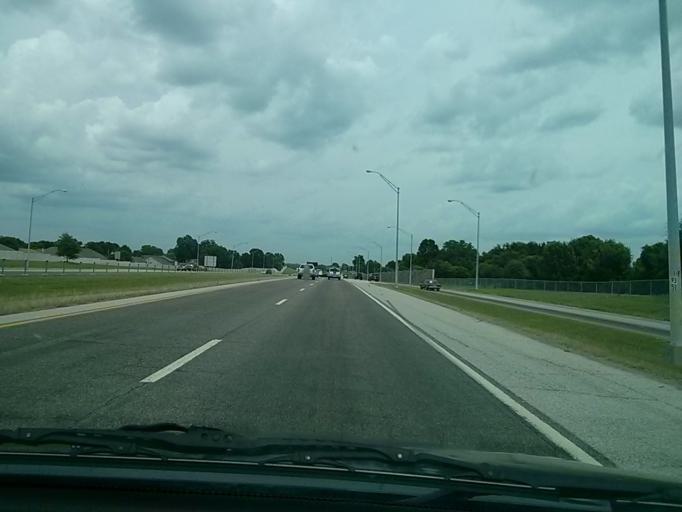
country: US
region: Oklahoma
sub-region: Tulsa County
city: Bixby
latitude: 36.0252
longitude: -95.8823
